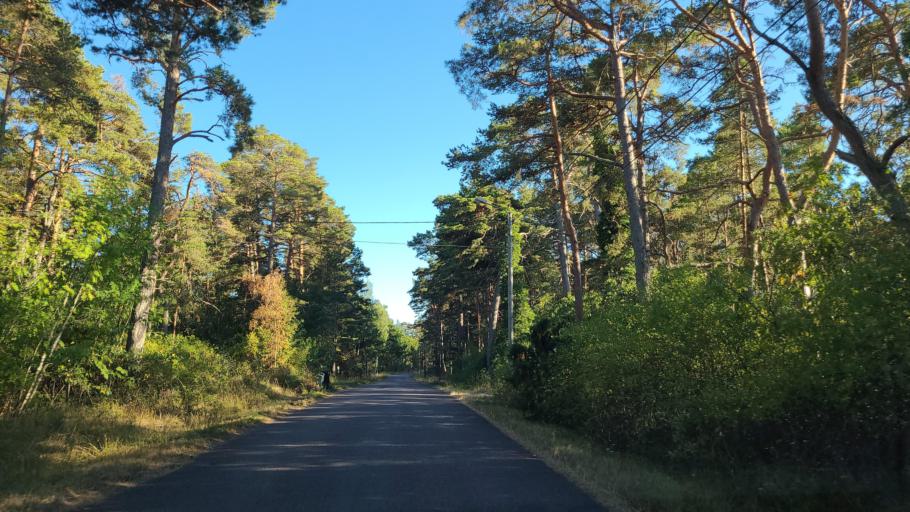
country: SE
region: Kalmar
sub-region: Vasterviks Kommun
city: Vaestervik
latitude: 57.3624
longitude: 17.0663
